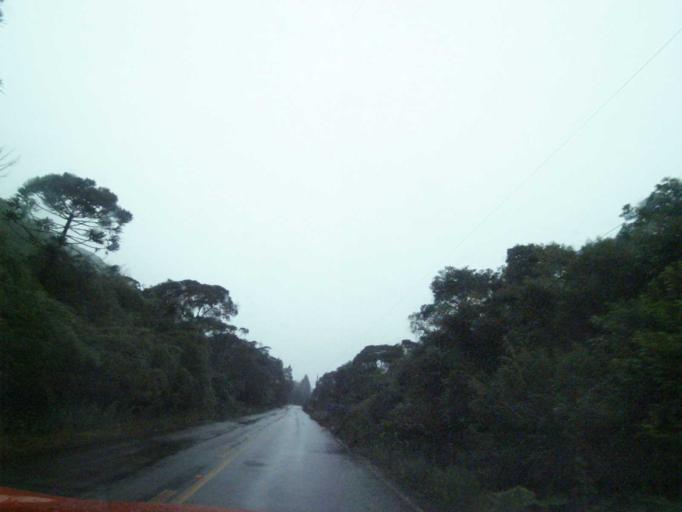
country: BR
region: Santa Catarina
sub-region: Anitapolis
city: Anitapolis
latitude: -27.7785
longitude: -49.0420
